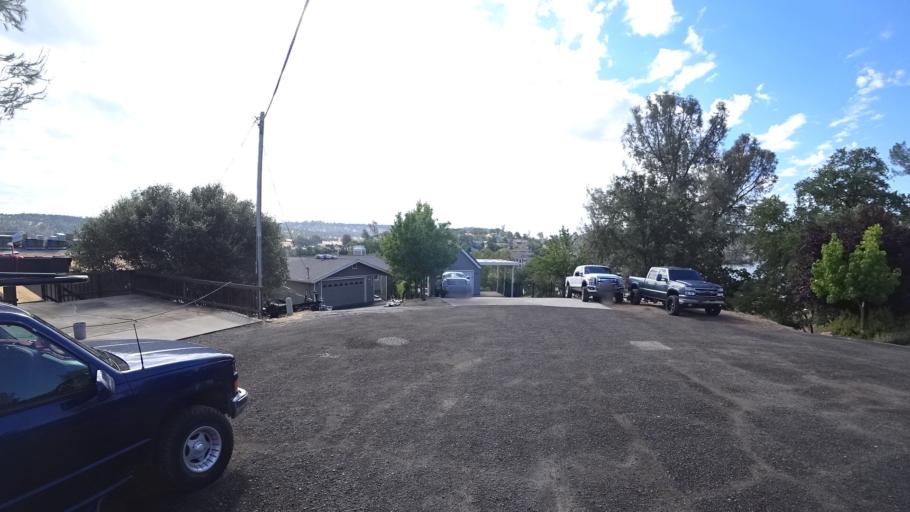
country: US
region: California
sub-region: Calaveras County
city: Copperopolis
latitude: 37.9145
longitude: -120.6021
